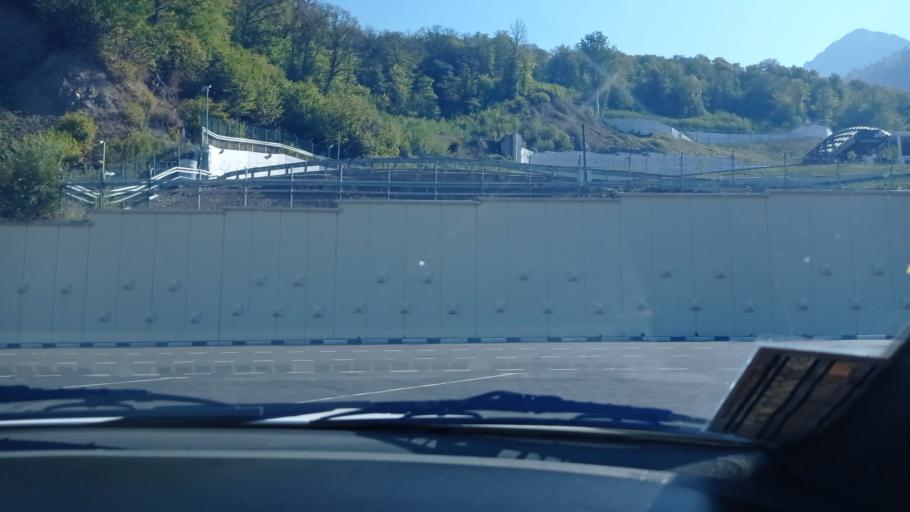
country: RU
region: Krasnodarskiy
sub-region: Sochi City
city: Krasnaya Polyana
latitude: 43.6790
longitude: 40.2421
